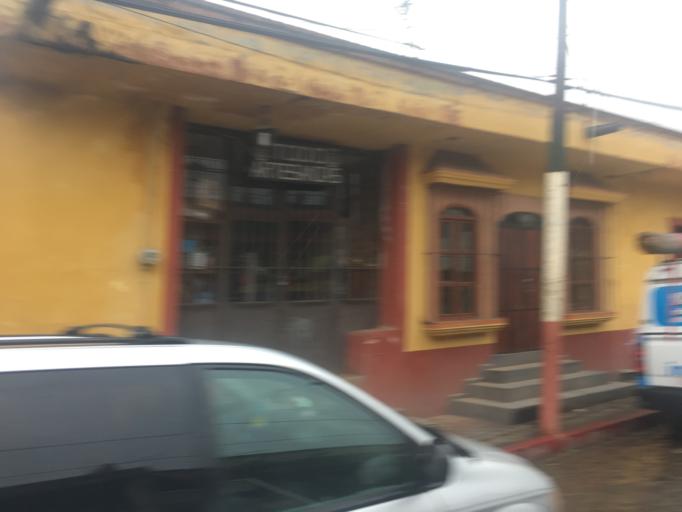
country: MX
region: Morelos
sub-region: Tlayacapan
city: Tlayacapan
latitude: 18.9545
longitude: -98.9818
